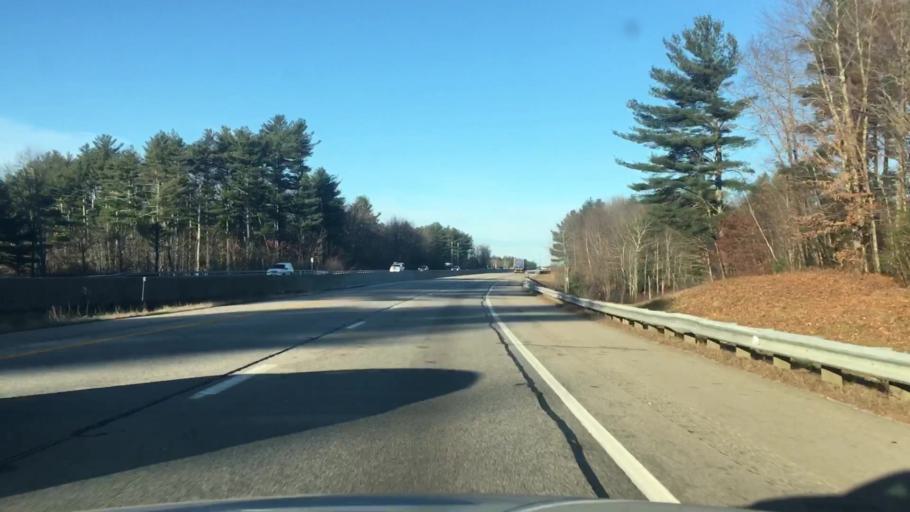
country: US
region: New Hampshire
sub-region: Rockingham County
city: Exeter
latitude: 43.0083
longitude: -71.0013
